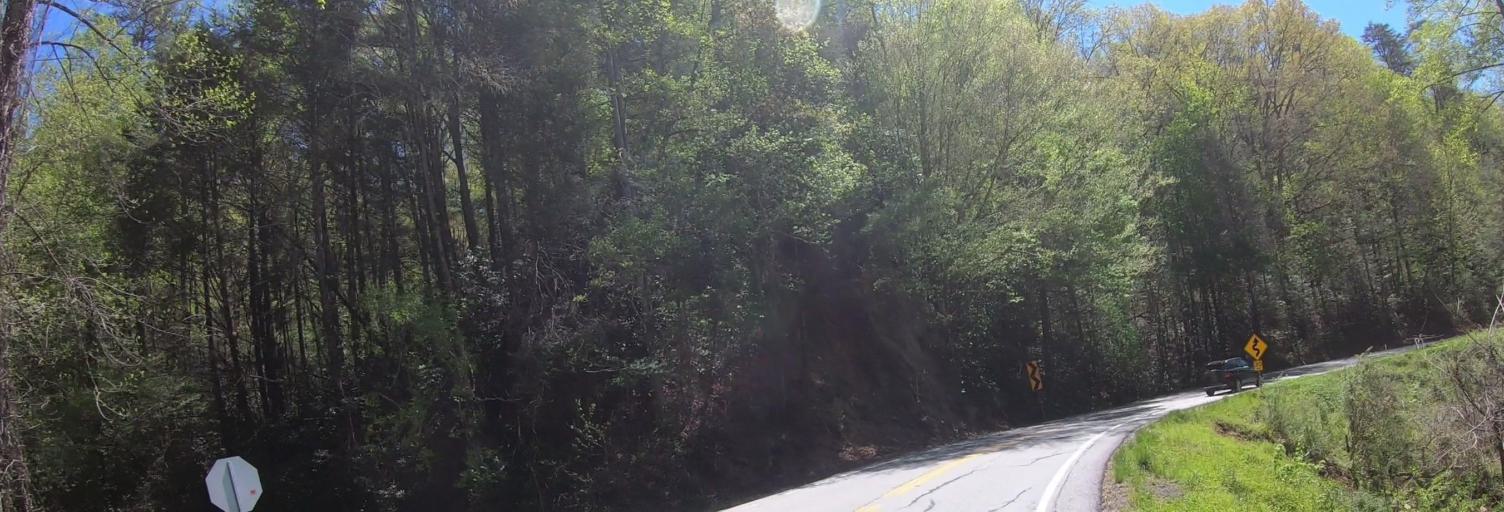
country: US
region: Georgia
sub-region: White County
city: Cleveland
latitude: 34.7229
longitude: -83.7479
